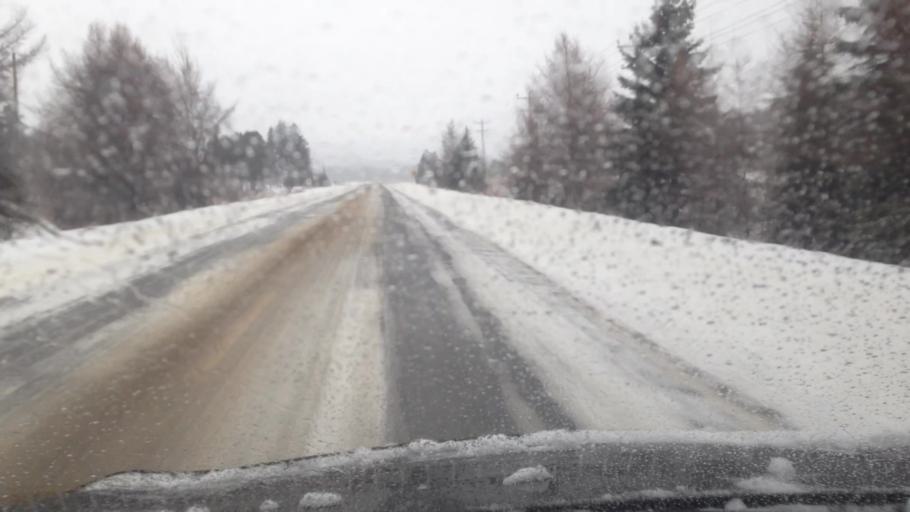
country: CA
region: Quebec
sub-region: Laurentides
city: Mont-Tremblant
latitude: 46.0566
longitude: -74.6183
